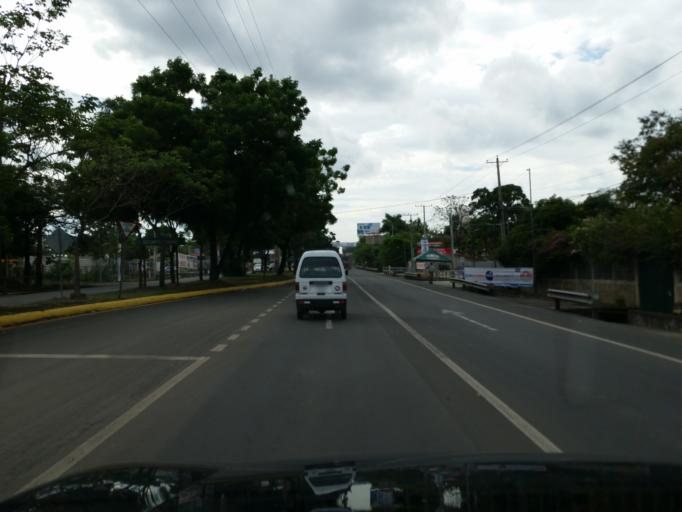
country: NI
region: Masaya
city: Ticuantepe
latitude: 12.0643
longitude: -86.2106
